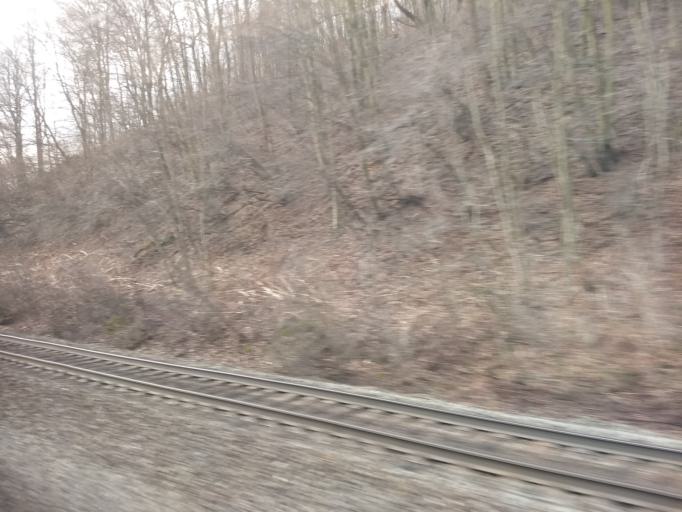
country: US
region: Pennsylvania
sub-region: Cambria County
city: Vinco
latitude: 40.3721
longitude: -78.8235
